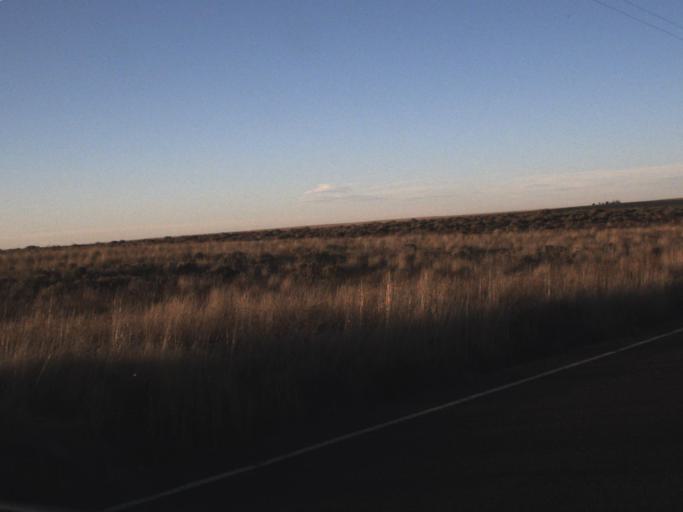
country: US
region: Washington
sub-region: Franklin County
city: Connell
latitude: 46.7668
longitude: -118.5475
